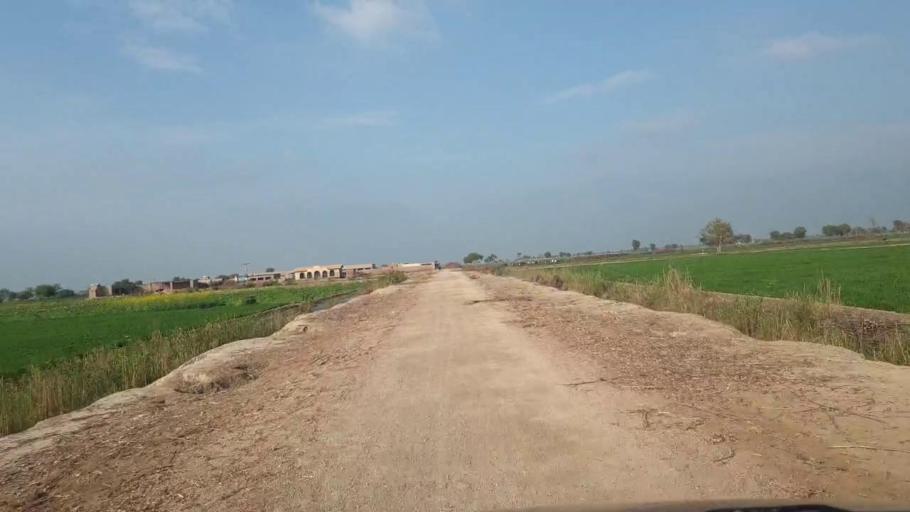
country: PK
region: Sindh
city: Shahdadpur
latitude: 25.8973
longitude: 68.6707
